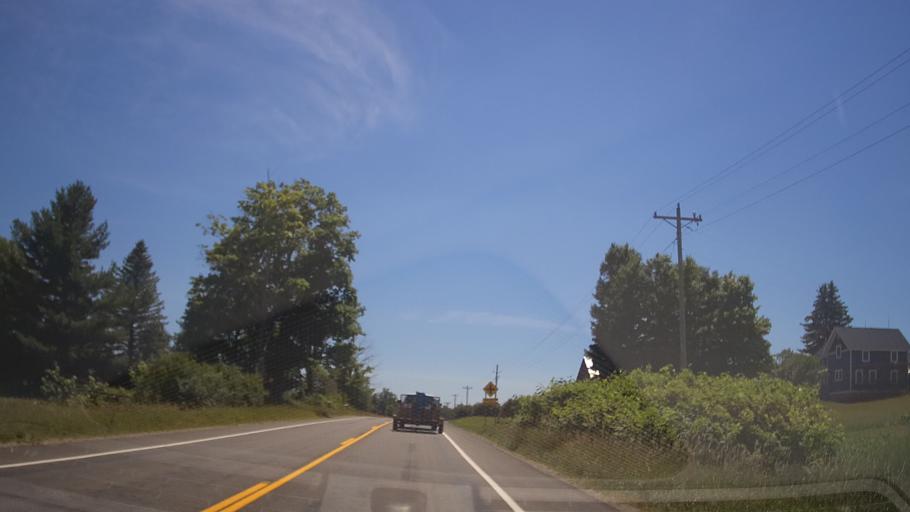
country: US
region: Michigan
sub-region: Grand Traverse County
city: Kingsley
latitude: 44.6029
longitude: -85.6964
